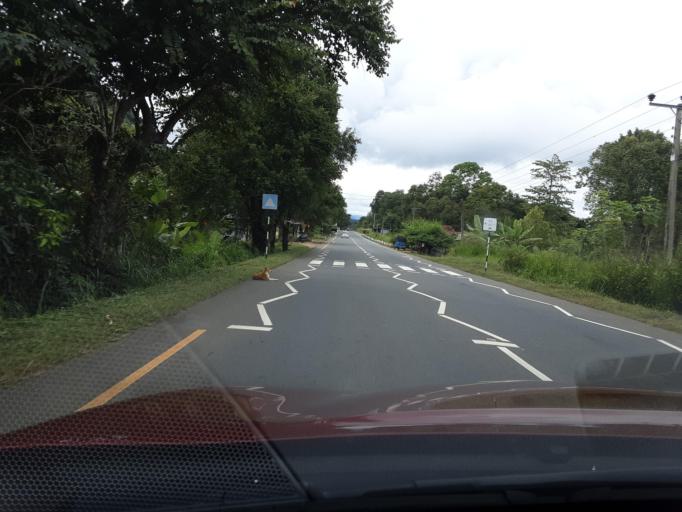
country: LK
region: Uva
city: Badulla
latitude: 7.3977
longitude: 81.1135
